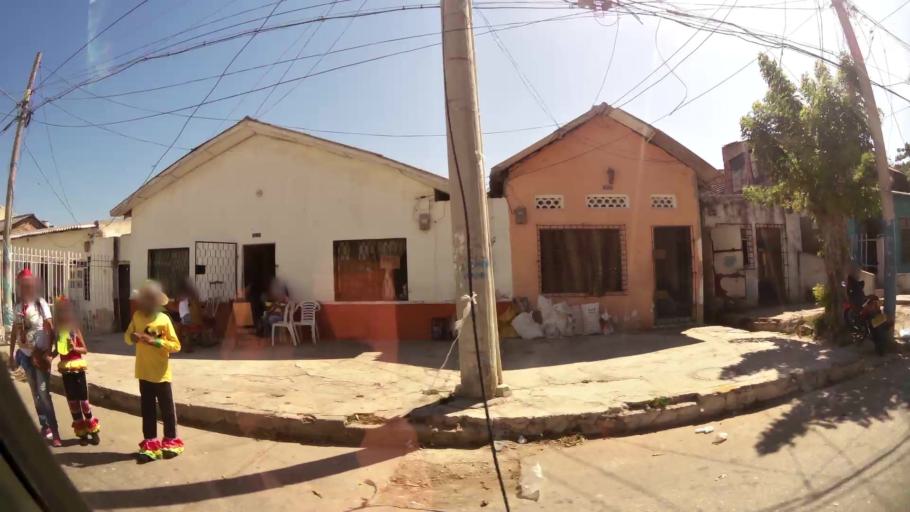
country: CO
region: Atlantico
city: Barranquilla
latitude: 10.9940
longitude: -74.7883
